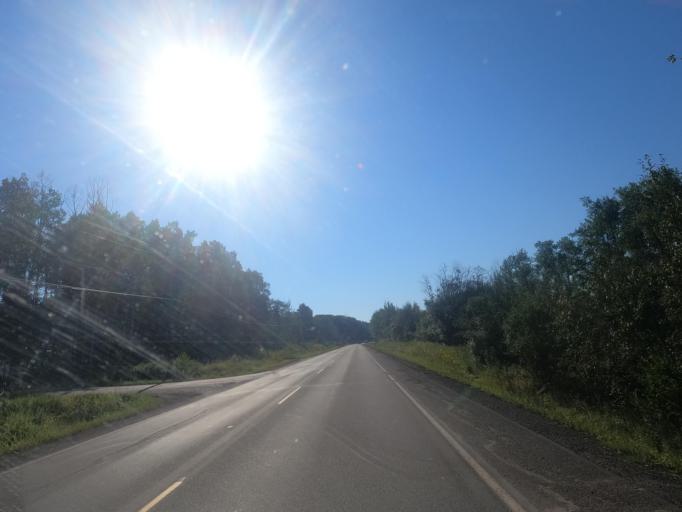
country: CA
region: British Columbia
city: Burns Lake
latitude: 54.3201
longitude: -125.8739
